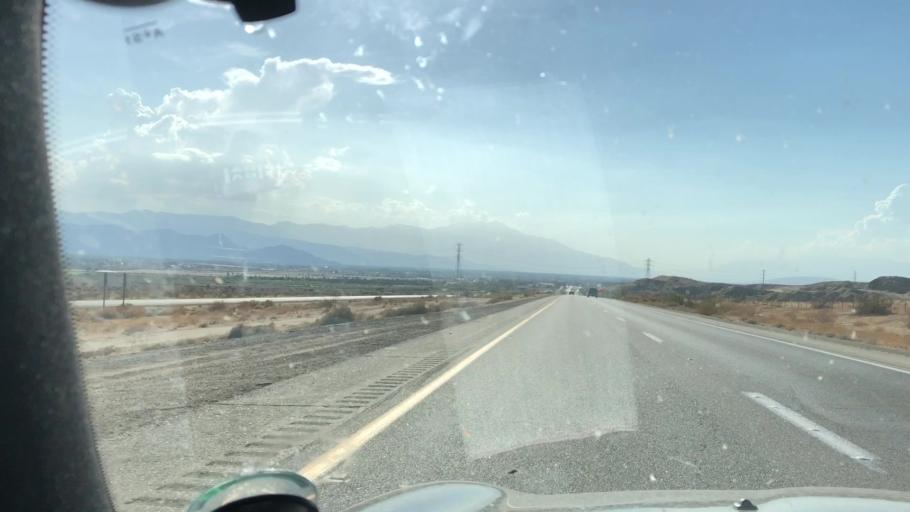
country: US
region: California
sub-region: Riverside County
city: Coachella
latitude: 33.7053
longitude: -116.1344
